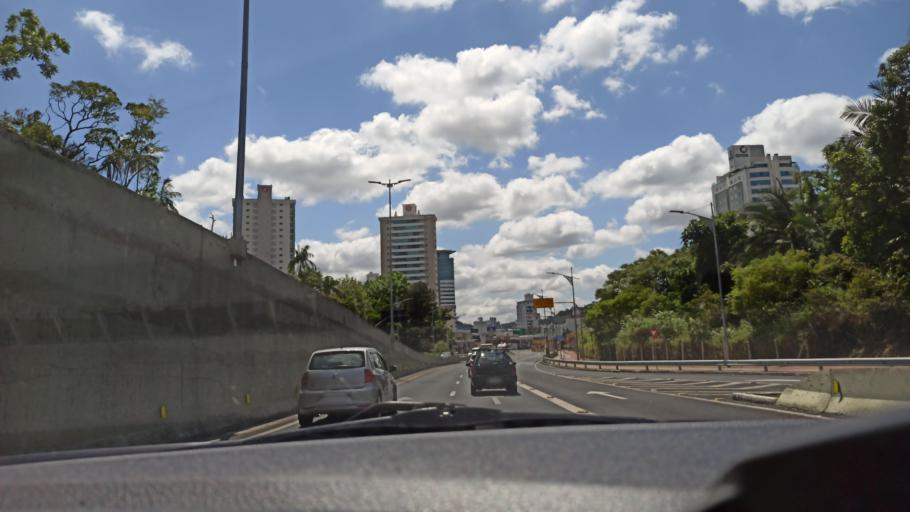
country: BR
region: Santa Catarina
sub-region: Blumenau
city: Blumenau
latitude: -26.9155
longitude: -49.0942
